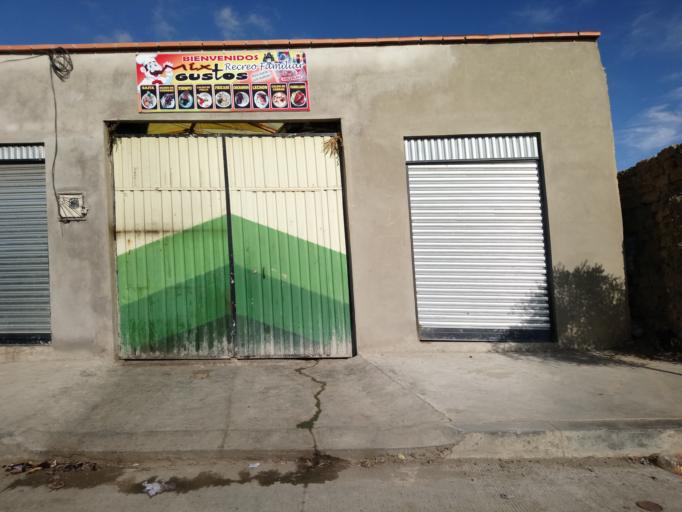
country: BO
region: La Paz
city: La Paz
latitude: -16.5031
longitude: -68.1996
